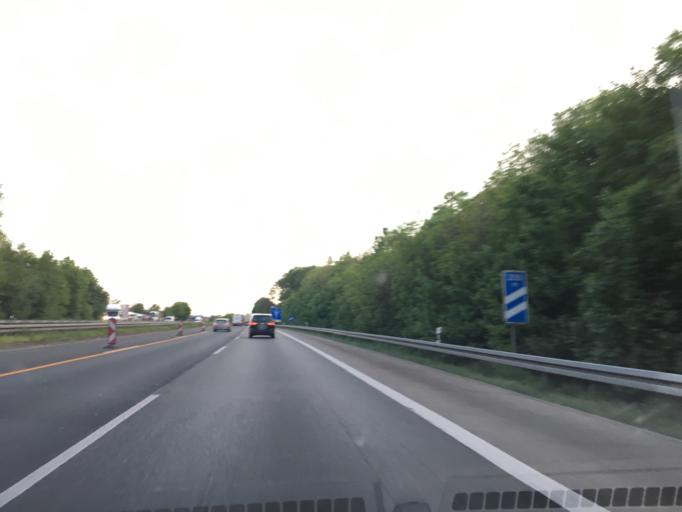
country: DE
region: Lower Saxony
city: Hasbergen
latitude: 52.2361
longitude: 7.8834
